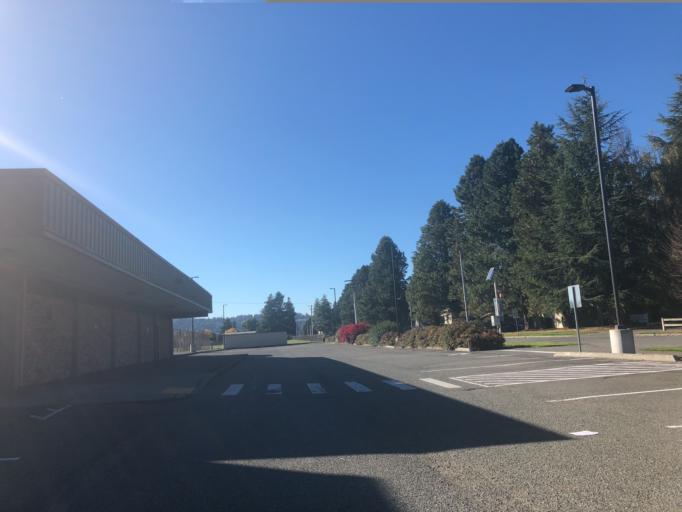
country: US
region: Washington
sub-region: King County
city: Auburn
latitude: 47.3300
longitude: -122.2143
